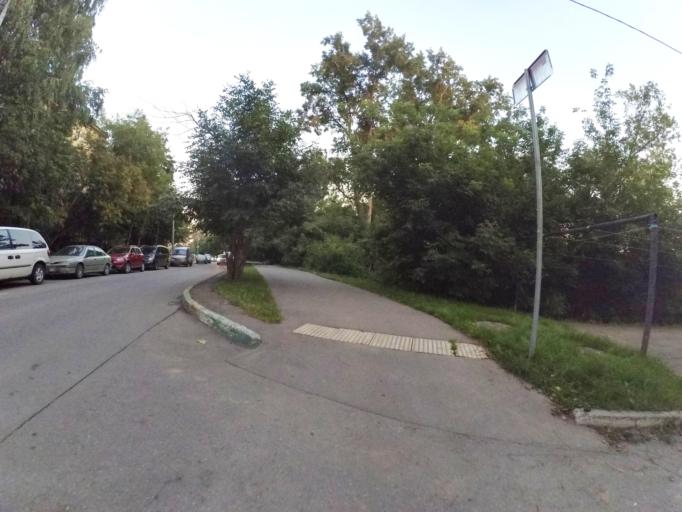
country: RU
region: Moscow
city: Strogino
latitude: 55.8434
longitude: 37.3997
